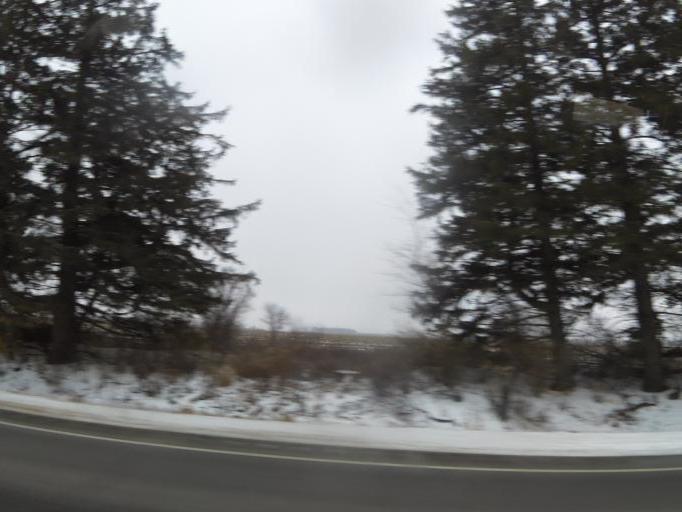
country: US
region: Minnesota
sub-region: Mower County
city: Grand Meadow
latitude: 43.7104
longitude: -92.5328
